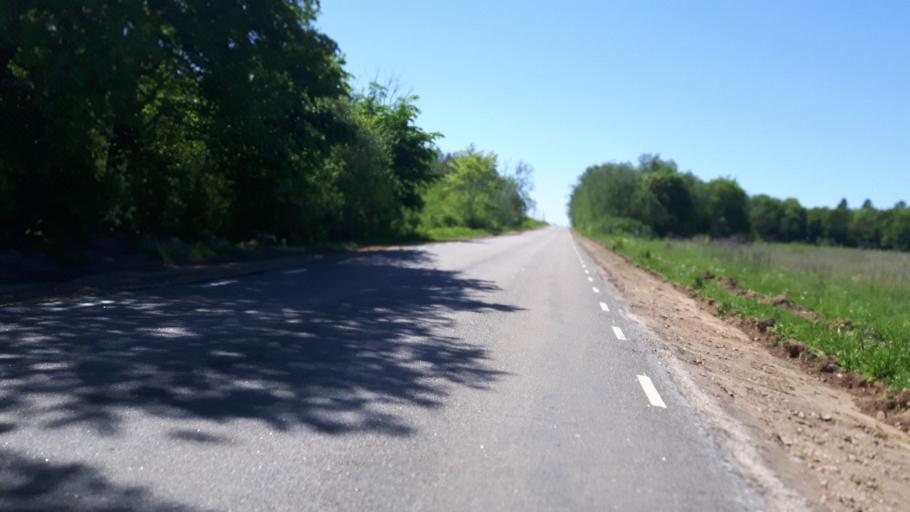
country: EE
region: Ida-Virumaa
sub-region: Narva-Joesuu linn
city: Narva-Joesuu
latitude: 59.4070
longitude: 27.9420
